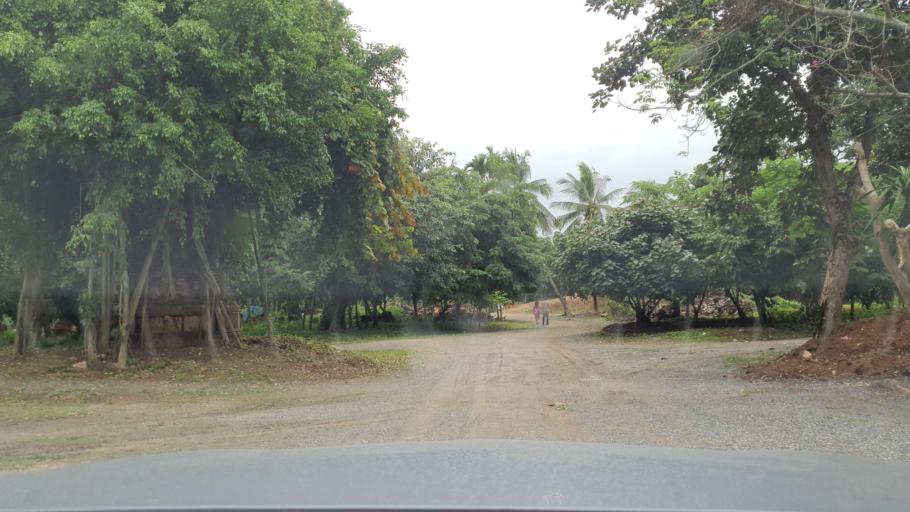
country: TH
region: Lamphun
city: Lamphun
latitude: 18.6055
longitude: 98.9769
